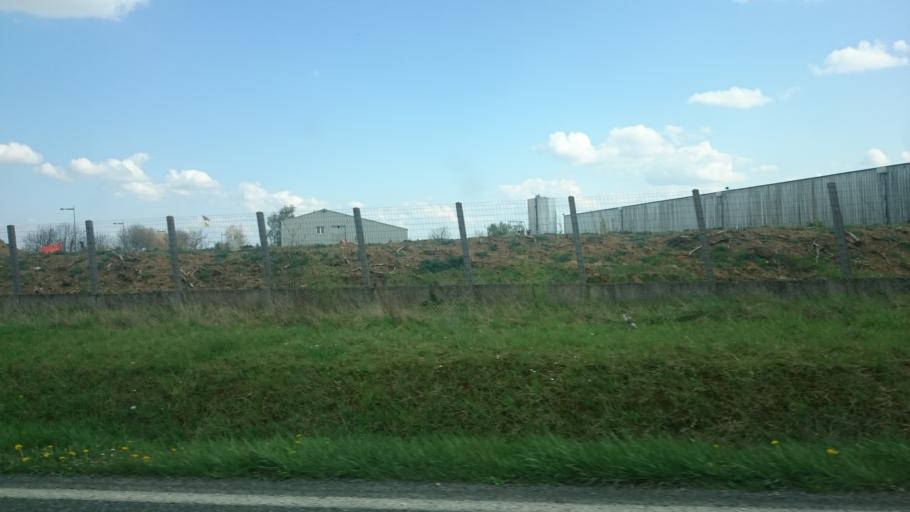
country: FR
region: Picardie
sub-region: Departement de l'Aisne
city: Gauchy
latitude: 49.8184
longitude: 3.2932
